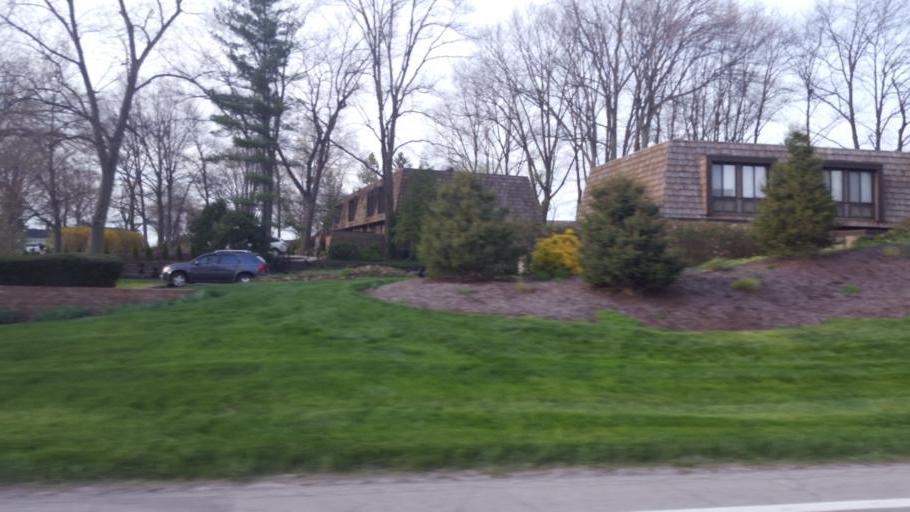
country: US
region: Ohio
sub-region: Erie County
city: Huron
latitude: 41.3873
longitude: -82.5286
